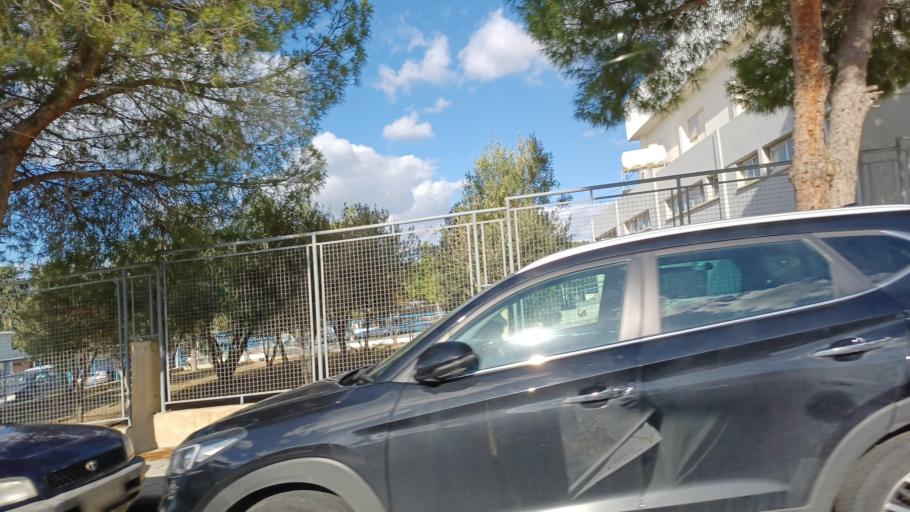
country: CY
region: Pafos
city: Empa
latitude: 34.7941
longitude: 32.4404
